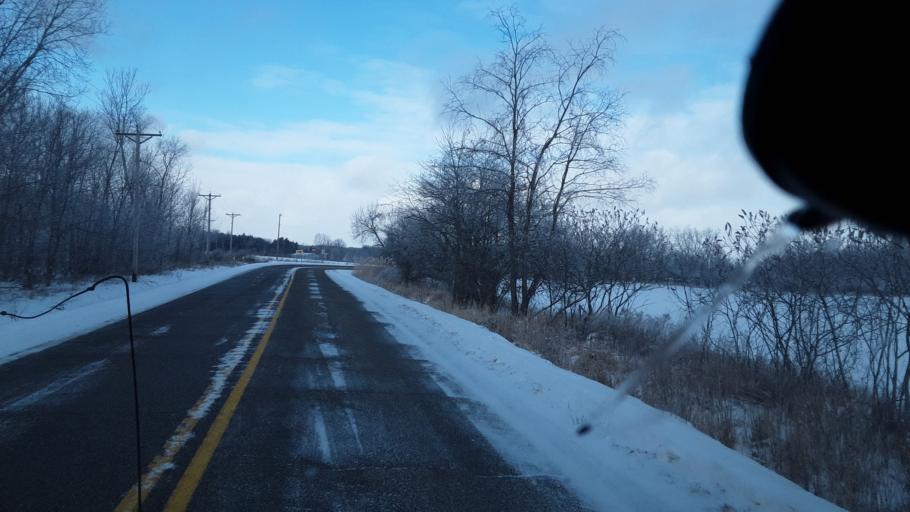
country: US
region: Michigan
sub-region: Eaton County
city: Eaton Rapids
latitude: 42.4904
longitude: -84.6241
